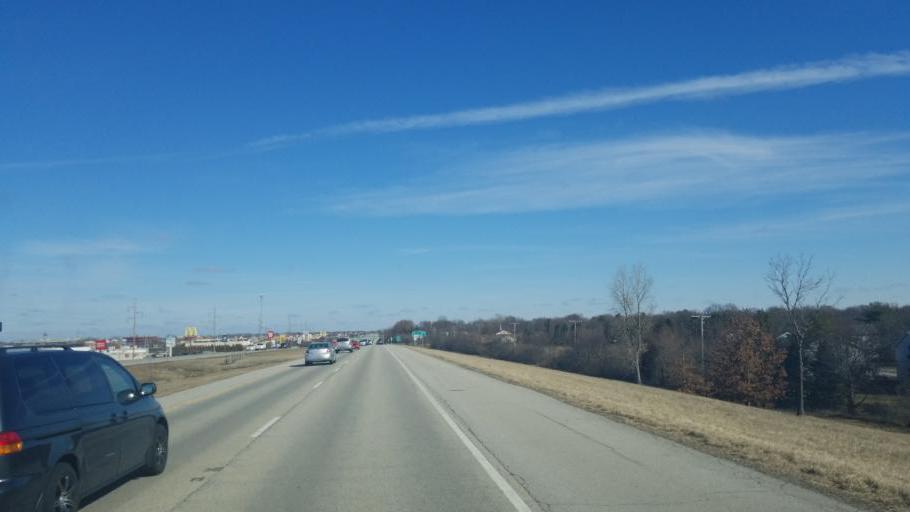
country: US
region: Illinois
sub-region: Sangamon County
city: Jerome
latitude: 39.7481
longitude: -89.7059
